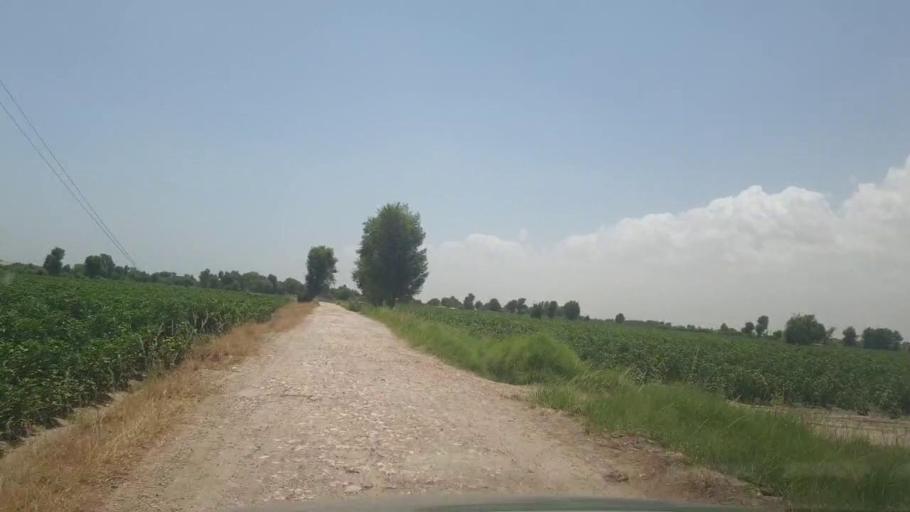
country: PK
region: Sindh
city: Kot Diji
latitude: 27.2694
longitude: 69.0199
